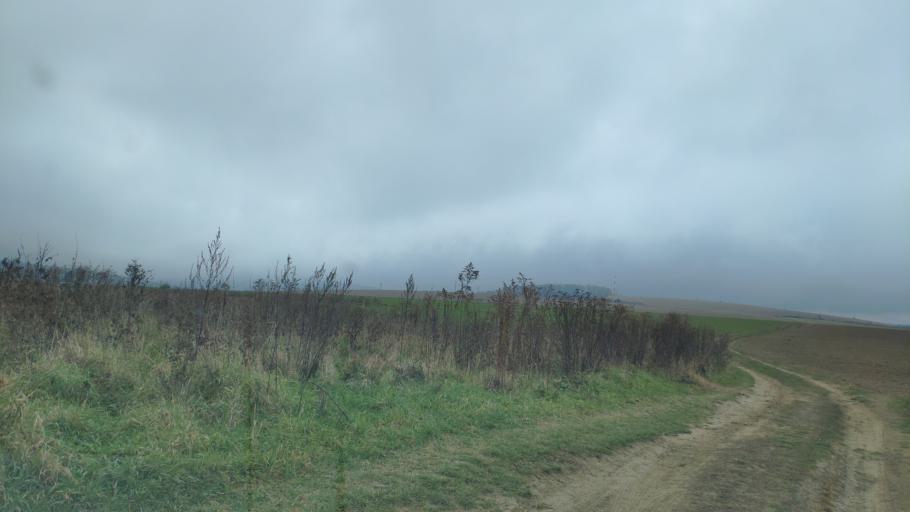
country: SK
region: Presovsky
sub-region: Okres Presov
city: Presov
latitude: 49.0134
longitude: 21.2107
